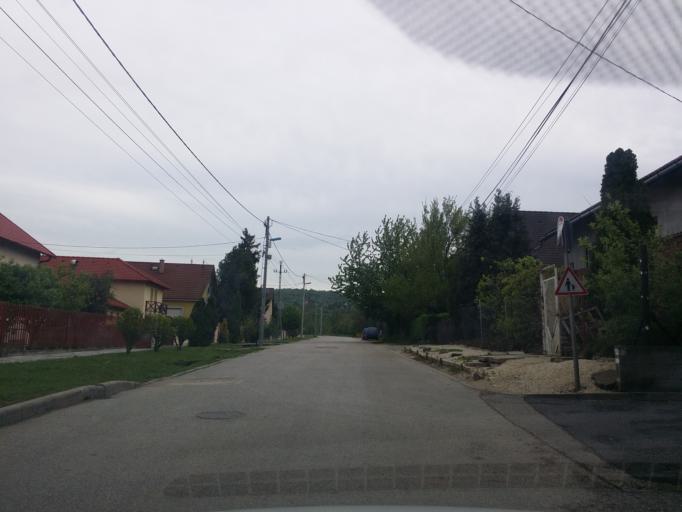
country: HU
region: Pest
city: Biatorbagy
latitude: 47.4782
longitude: 18.8329
